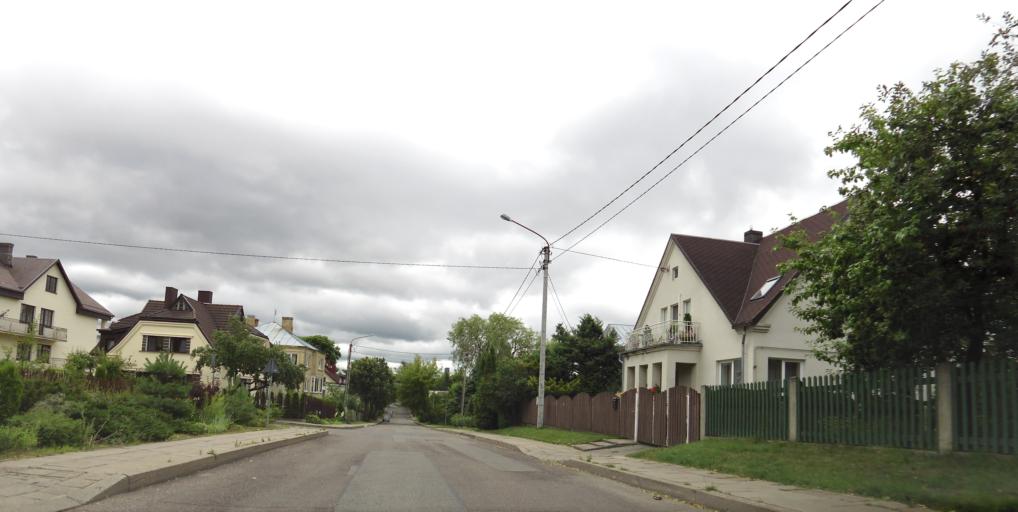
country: LT
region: Vilnius County
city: Seskine
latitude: 54.6966
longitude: 25.2456
